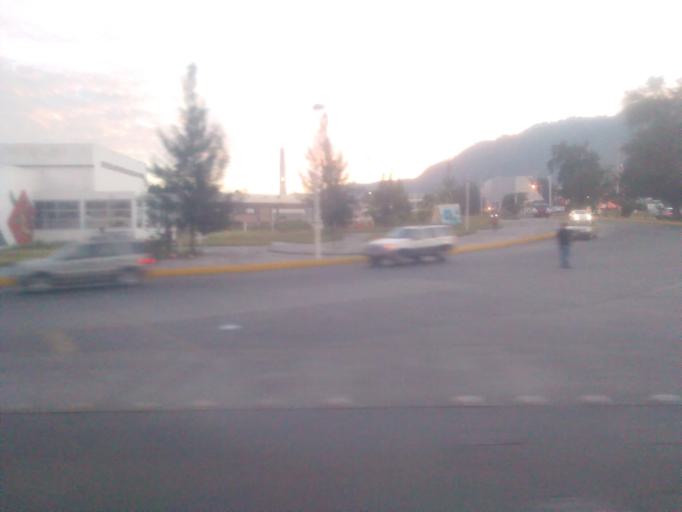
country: MX
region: Nayarit
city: Tepic
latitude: 21.5127
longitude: -104.9026
